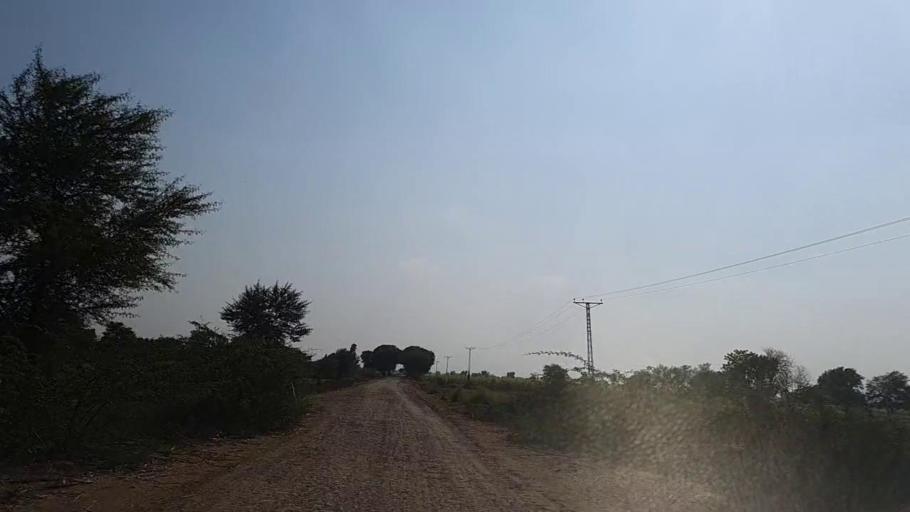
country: PK
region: Sindh
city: Daur
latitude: 26.4509
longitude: 68.2347
